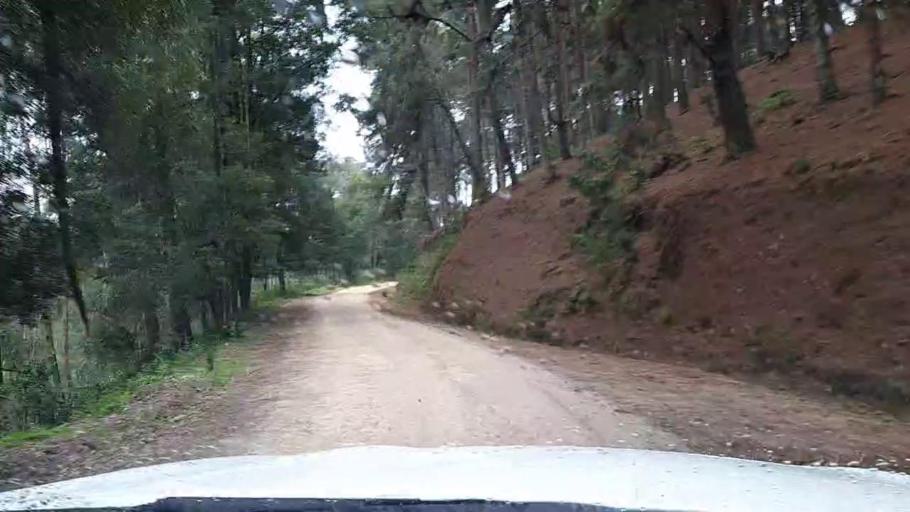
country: RW
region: Southern Province
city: Nzega
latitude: -2.3624
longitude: 29.3821
